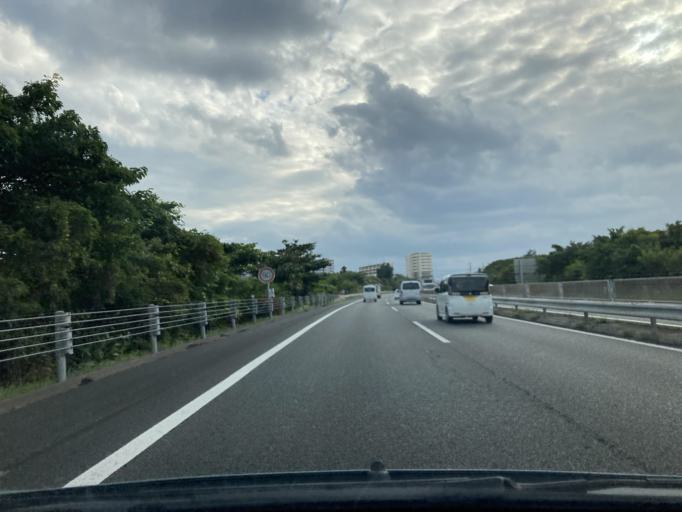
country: JP
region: Okinawa
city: Ginowan
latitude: 26.2615
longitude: 127.7717
